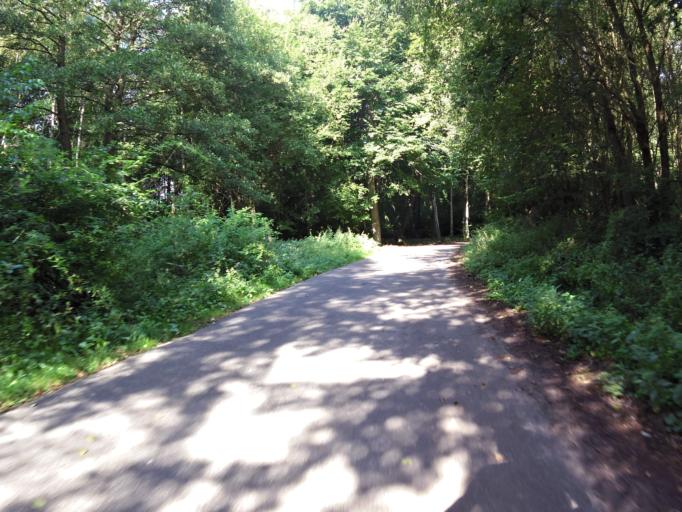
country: DE
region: Mecklenburg-Vorpommern
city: Seebad Bansin
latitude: 53.9921
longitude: 14.1125
